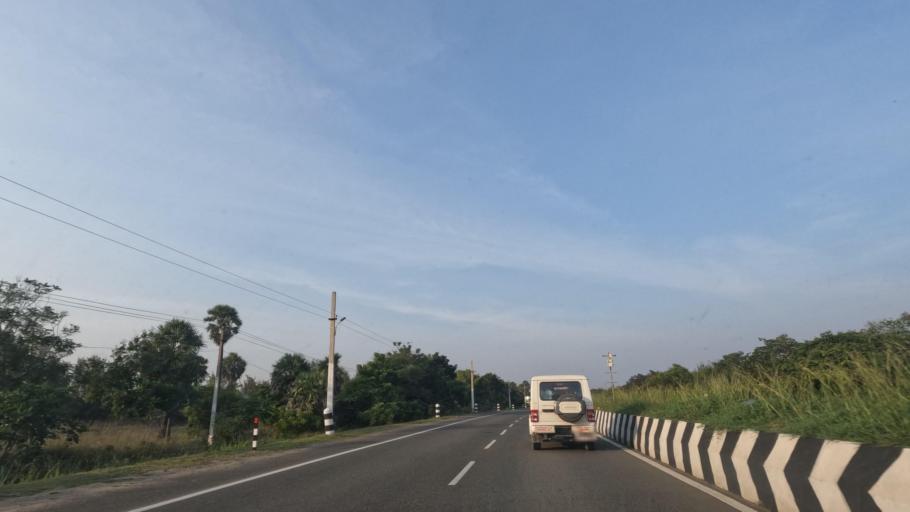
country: IN
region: Tamil Nadu
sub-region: Kancheepuram
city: Mamallapuram
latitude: 12.6685
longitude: 80.2102
